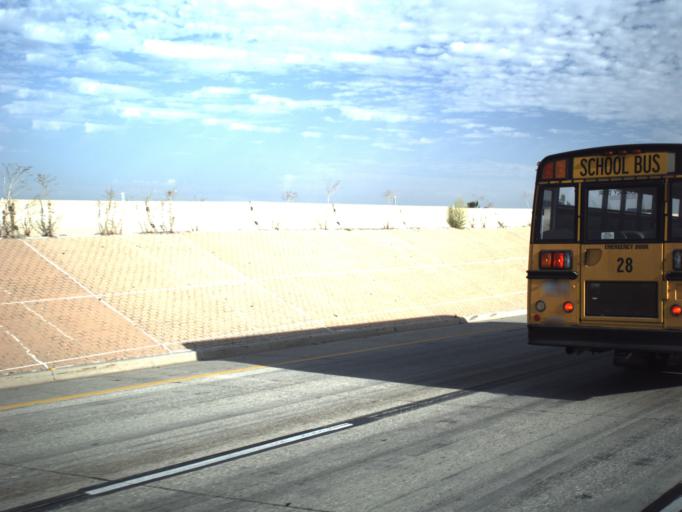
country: US
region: Utah
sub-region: Salt Lake County
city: Salt Lake City
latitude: 40.7386
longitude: -111.9488
